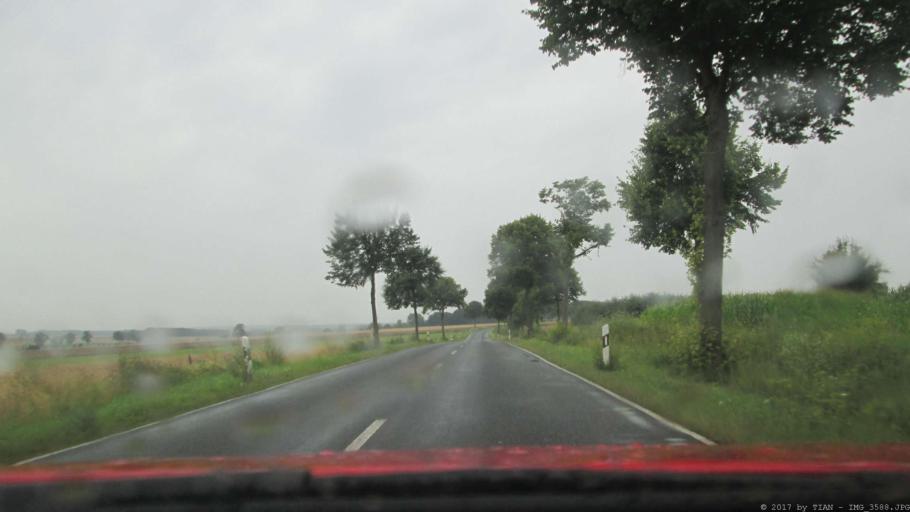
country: DE
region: Lower Saxony
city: Konigslutter am Elm
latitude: 52.3410
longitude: 10.8183
